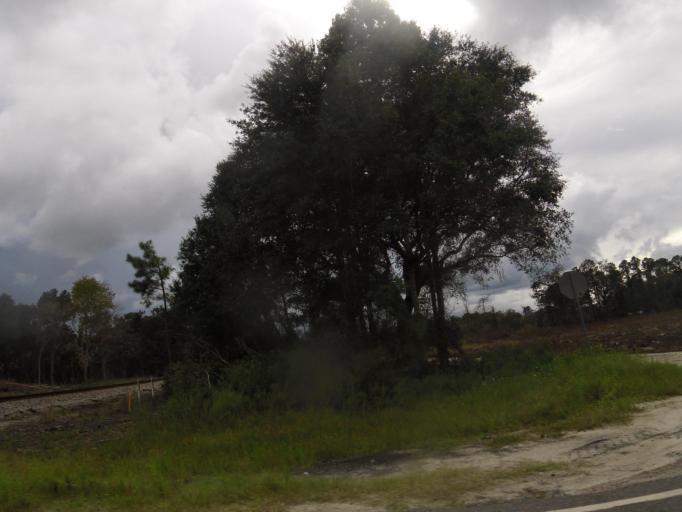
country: US
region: Florida
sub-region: Baker County
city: Macclenny
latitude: 30.5175
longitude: -82.2243
